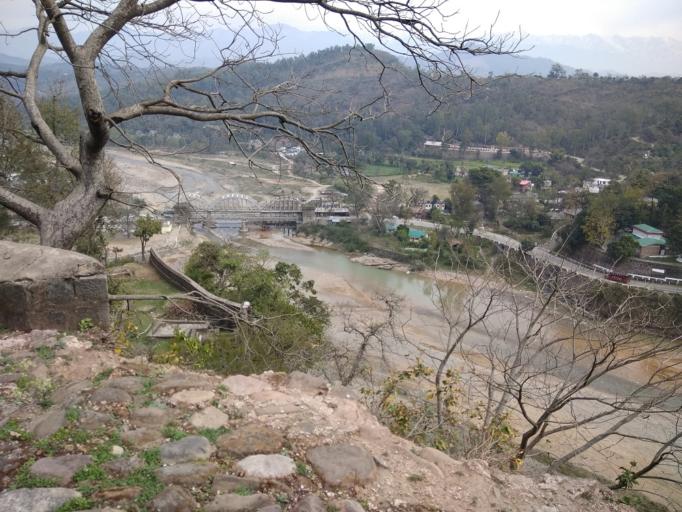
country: IN
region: Himachal Pradesh
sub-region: Kangra
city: Kotla
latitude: 32.2353
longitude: 76.0455
